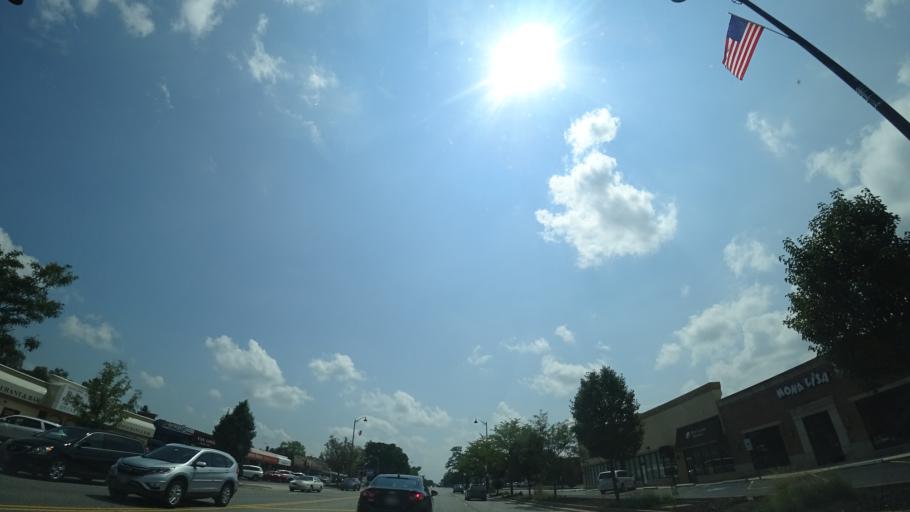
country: US
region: Illinois
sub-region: Cook County
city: Palos Heights
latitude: 41.6671
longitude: -87.7966
